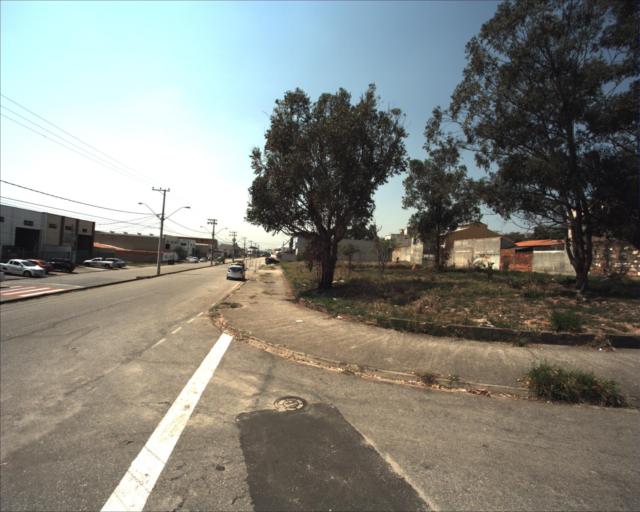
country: BR
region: Sao Paulo
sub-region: Sorocaba
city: Sorocaba
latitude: -23.4361
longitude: -47.4824
